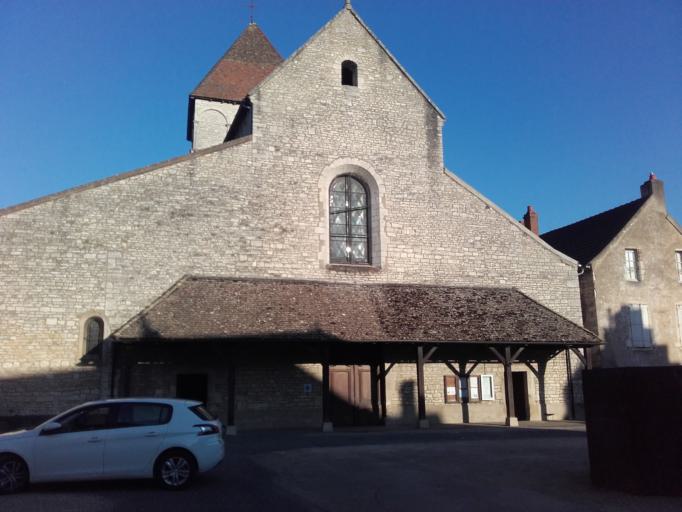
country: FR
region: Bourgogne
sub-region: Departement de Saone-et-Loire
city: Chagny
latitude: 46.9121
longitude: 4.7520
